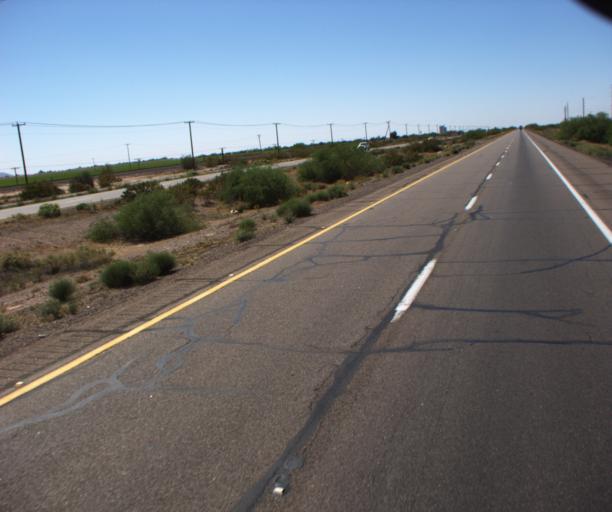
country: US
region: Arizona
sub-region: Maricopa County
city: Gila Bend
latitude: 32.9391
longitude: -112.7609
